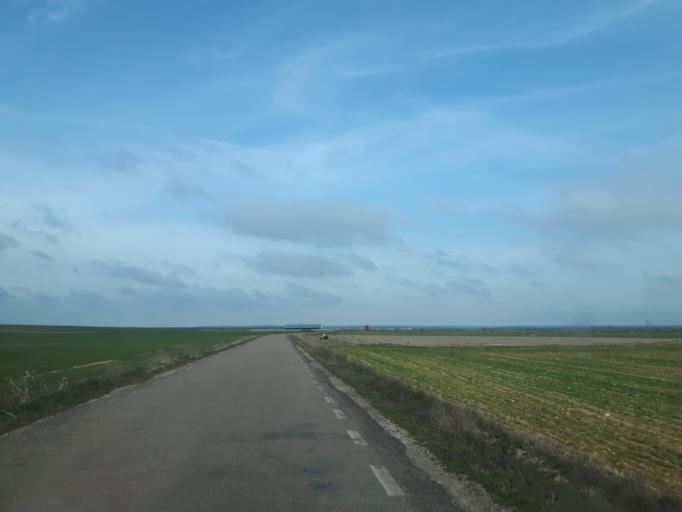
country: ES
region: Castille and Leon
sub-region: Provincia de Salamanca
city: Coca de Alba
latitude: 40.8630
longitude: -5.3684
